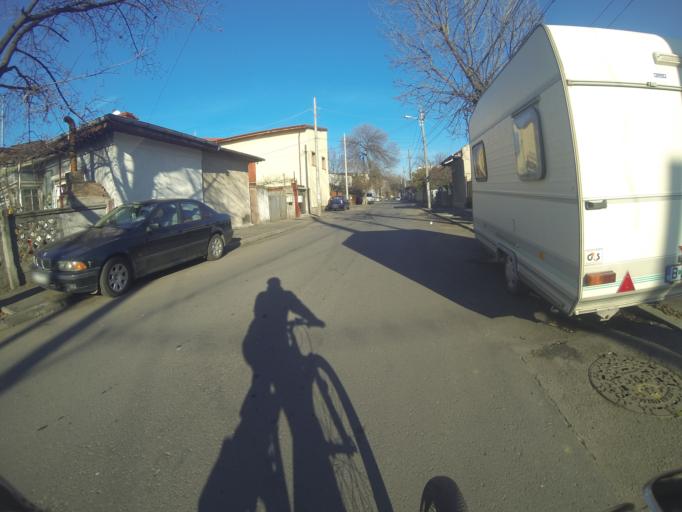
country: RO
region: Bucuresti
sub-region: Municipiul Bucuresti
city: Bucuresti
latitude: 44.4022
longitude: 26.0699
